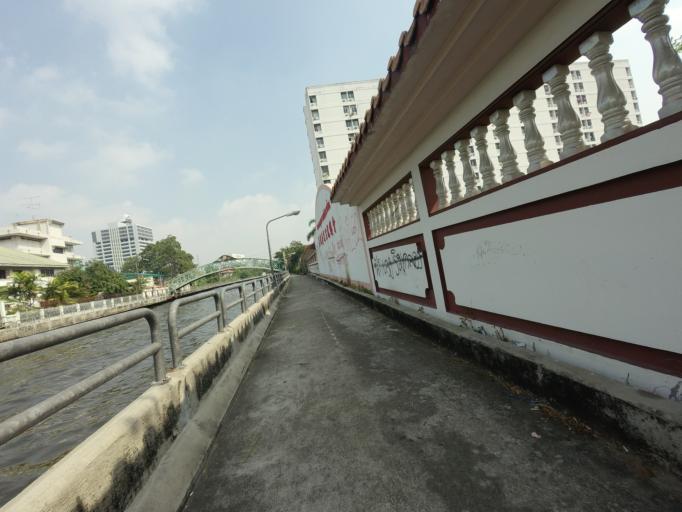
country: TH
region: Bangkok
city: Watthana
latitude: 13.7447
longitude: 100.5993
